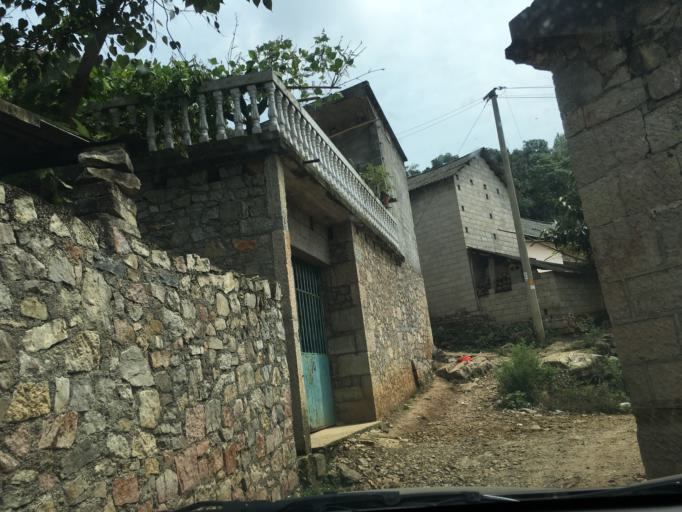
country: CN
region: Guizhou Sheng
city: Anshun
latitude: 25.5968
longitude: 105.6749
